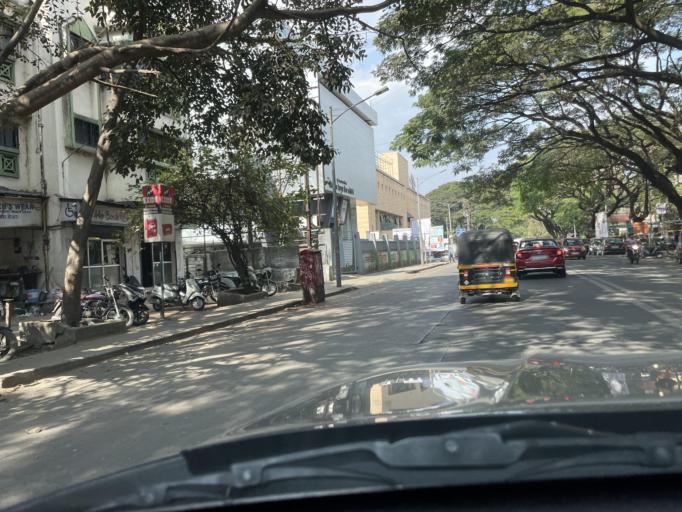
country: IN
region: Maharashtra
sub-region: Pune Division
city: Pune
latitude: 18.4964
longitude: 73.9001
